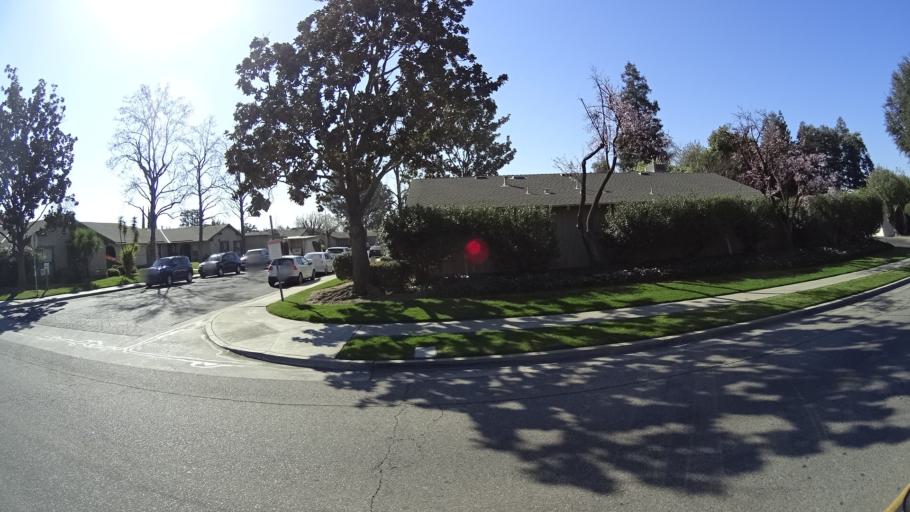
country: US
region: California
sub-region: Fresno County
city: Clovis
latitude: 36.8302
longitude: -119.7713
